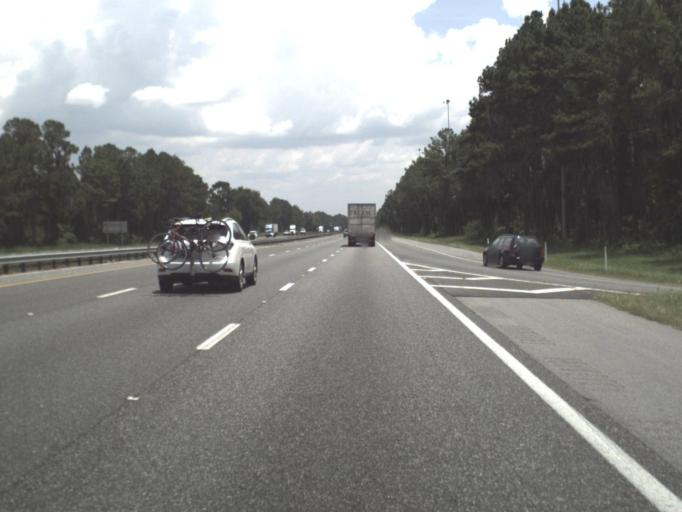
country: US
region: Florida
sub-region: Hamilton County
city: Jasper
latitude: 30.4470
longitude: -82.9304
